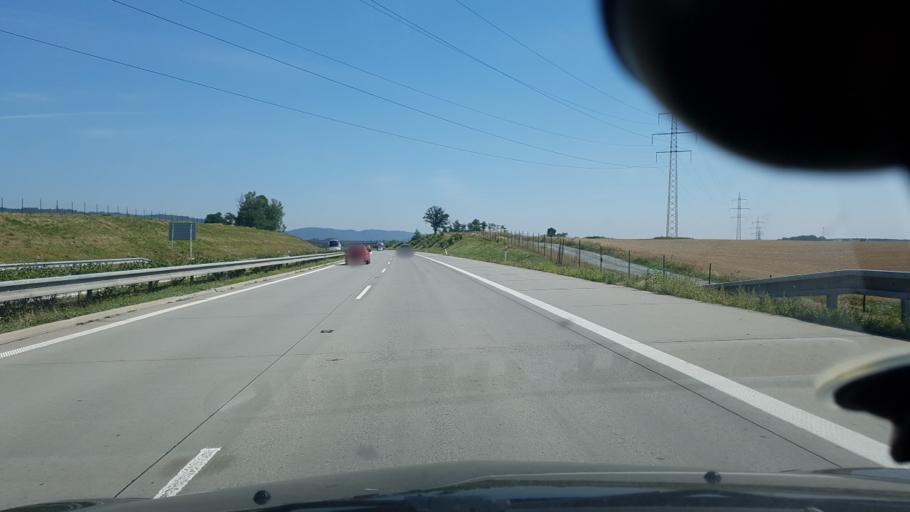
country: CZ
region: Olomoucky
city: Belotin
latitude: 49.5964
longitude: 17.7904
